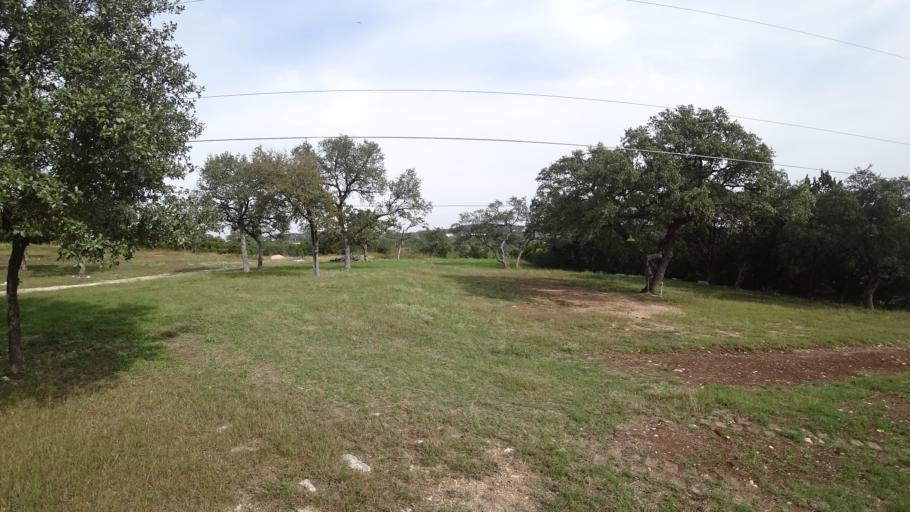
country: US
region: Texas
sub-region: Travis County
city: Hudson Bend
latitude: 30.3927
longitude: -97.9298
